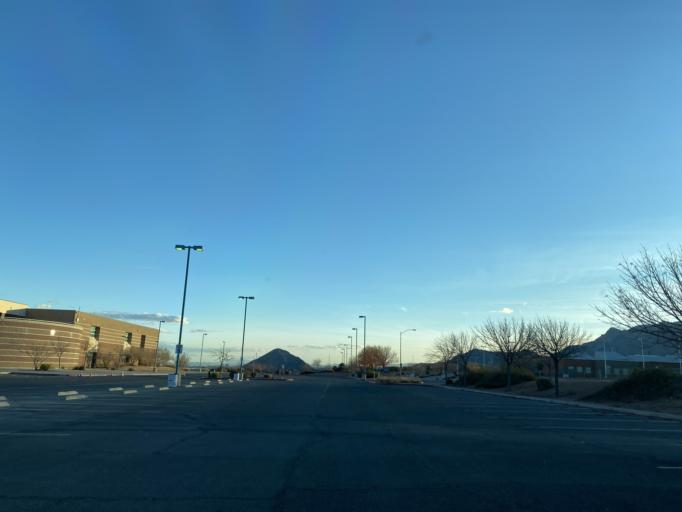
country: US
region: Nevada
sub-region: Clark County
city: Summerlin South
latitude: 36.2798
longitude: -115.3209
